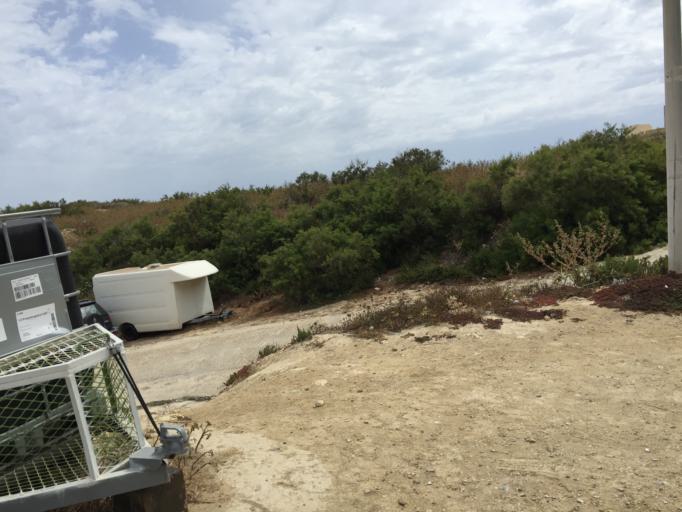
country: MT
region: Iz-Zebbug
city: Zebbug
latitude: 36.0783
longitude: 14.2491
